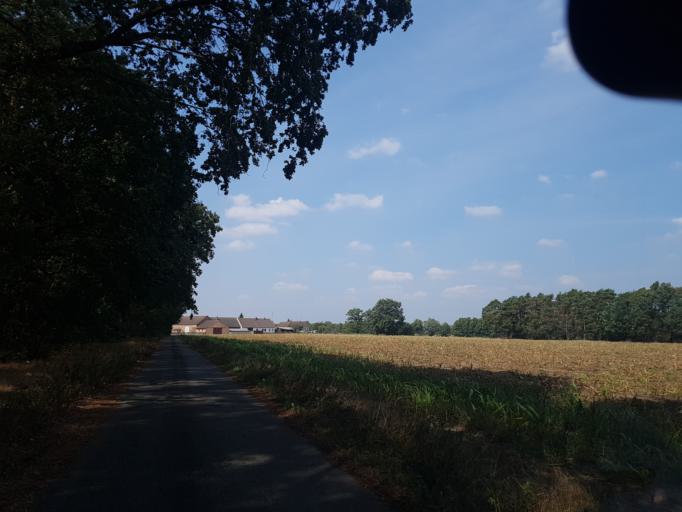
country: DE
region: Saxony-Anhalt
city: Lindau
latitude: 52.0677
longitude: 12.2536
